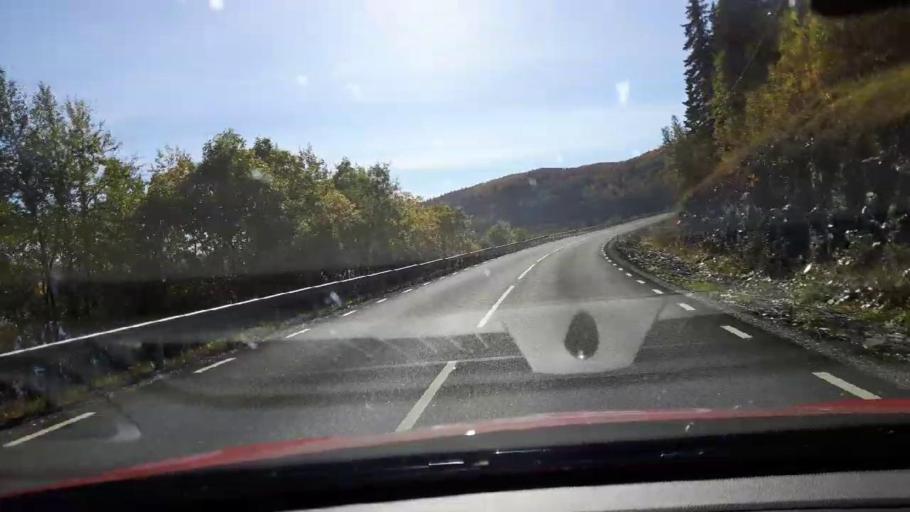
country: NO
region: Nord-Trondelag
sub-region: Royrvik
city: Royrvik
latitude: 64.8252
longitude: 14.0777
